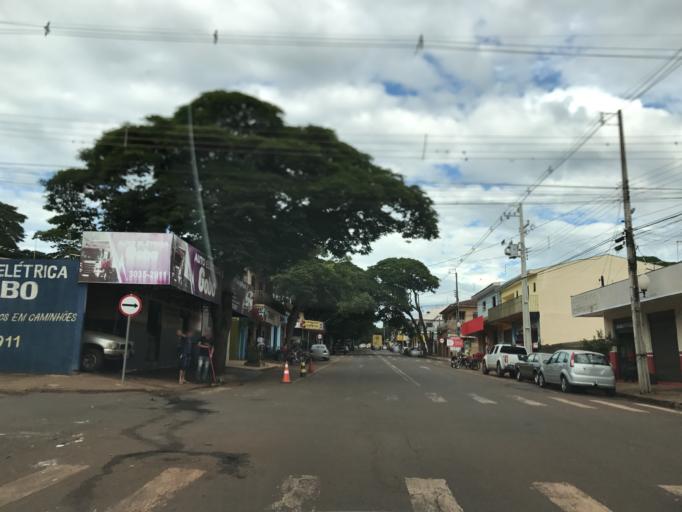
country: BR
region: Parana
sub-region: Sarandi
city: Sarandi
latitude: -23.4351
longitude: -51.8697
